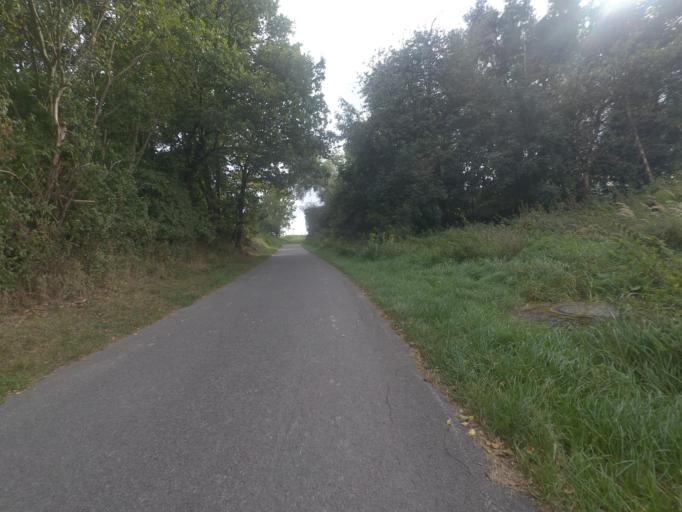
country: DE
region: North Rhine-Westphalia
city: Iserlohn
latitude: 51.4268
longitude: 7.6668
